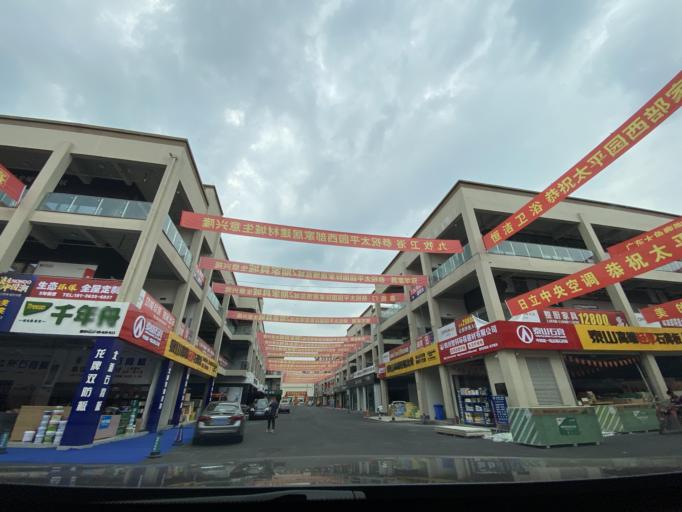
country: CN
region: Sichuan
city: Dongsheng
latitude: 30.6091
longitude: 103.9403
